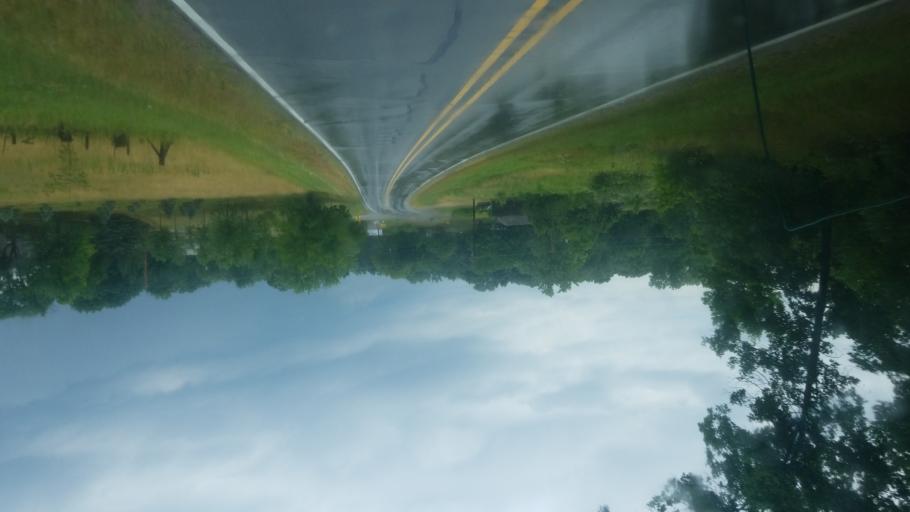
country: US
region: Indiana
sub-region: Steuben County
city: Hamilton
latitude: 41.5153
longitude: -84.8730
